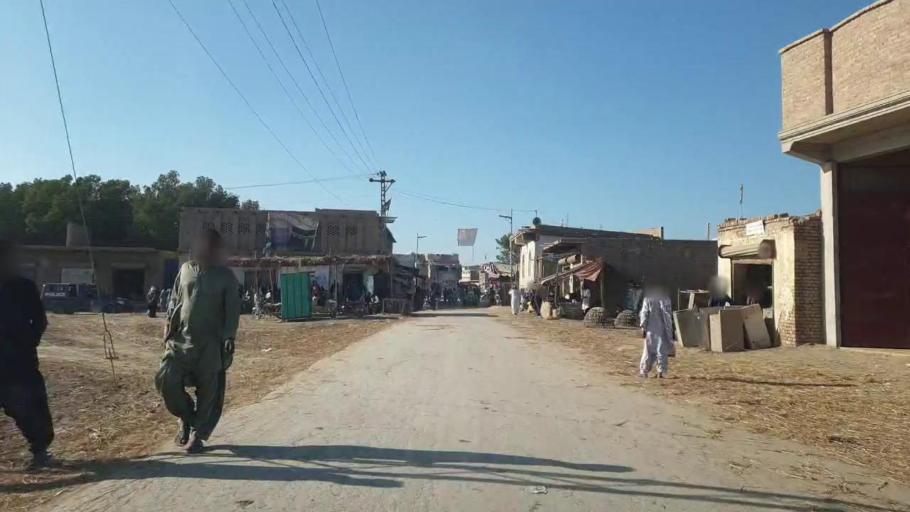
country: PK
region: Sindh
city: New Badah
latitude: 27.3272
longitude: 68.0286
